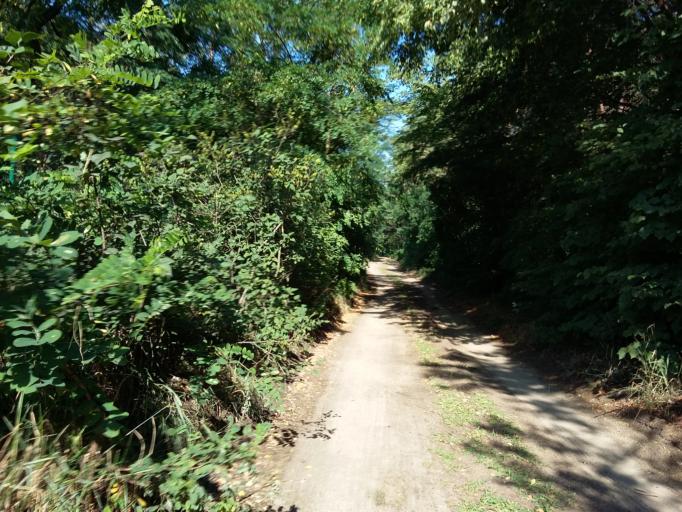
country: AT
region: Lower Austria
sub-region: Politischer Bezirk Ganserndorf
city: Drosing
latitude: 48.4979
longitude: 16.9538
